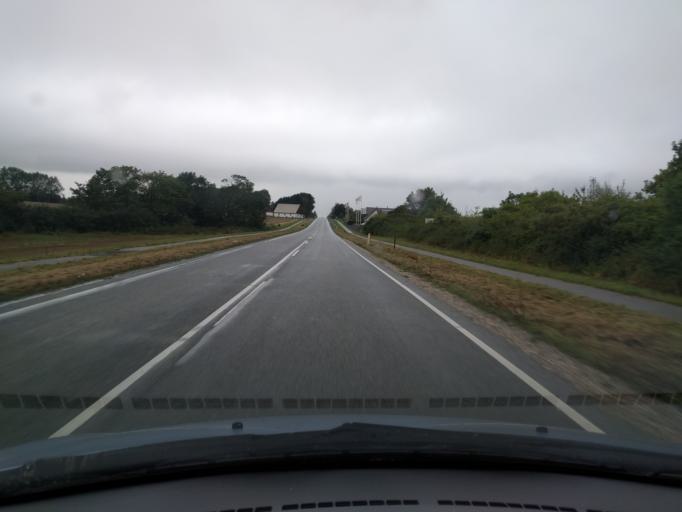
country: DK
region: Zealand
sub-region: Naestved Kommune
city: Naestved
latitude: 55.1911
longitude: 11.7727
